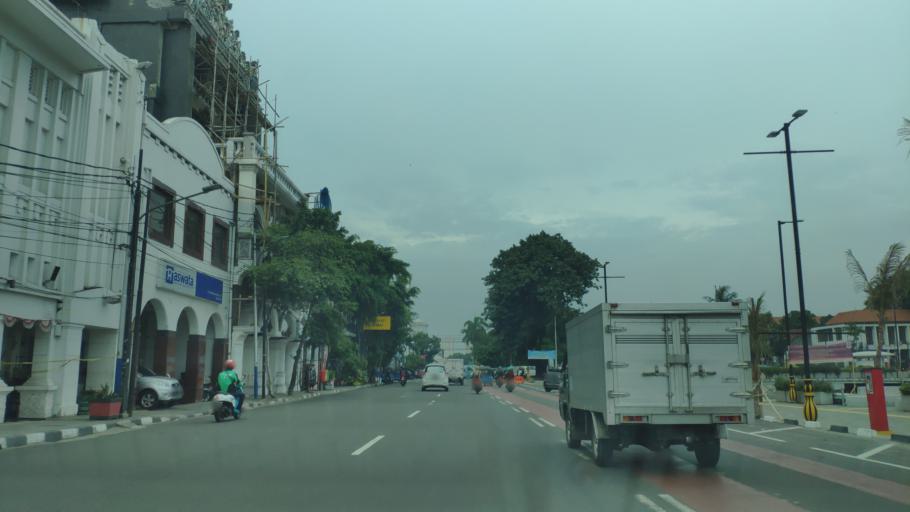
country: ID
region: Jakarta Raya
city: Jakarta
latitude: -6.1352
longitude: 106.8113
